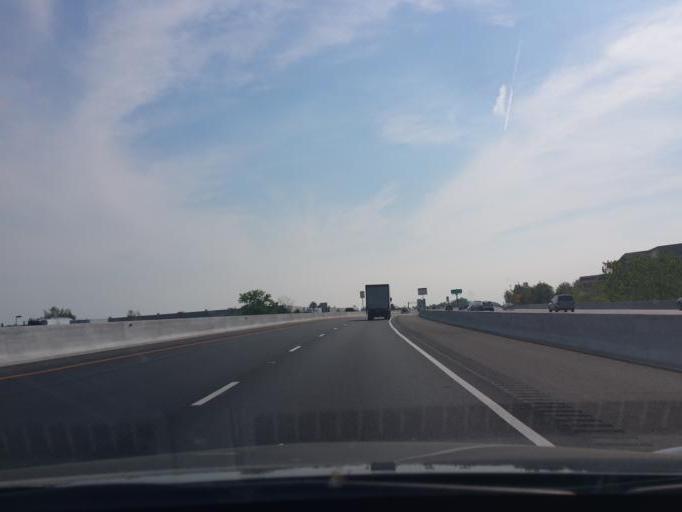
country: US
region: Maryland
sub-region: Baltimore County
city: White Marsh
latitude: 39.3734
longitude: -76.4554
